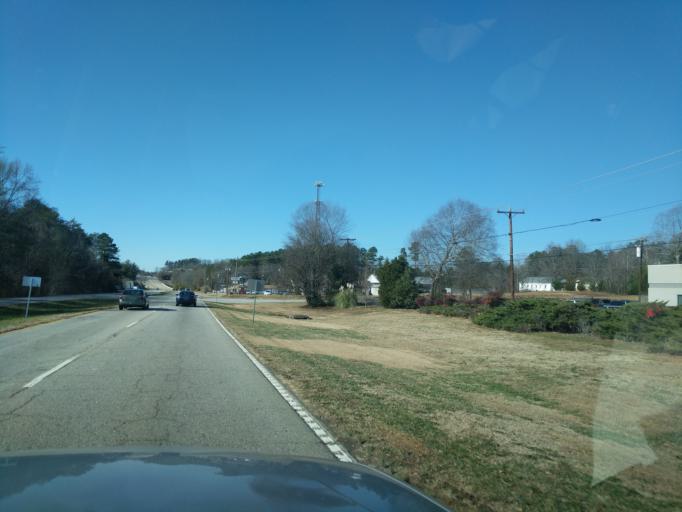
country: US
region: South Carolina
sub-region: Greenville County
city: Parker
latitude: 34.8330
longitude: -82.4775
